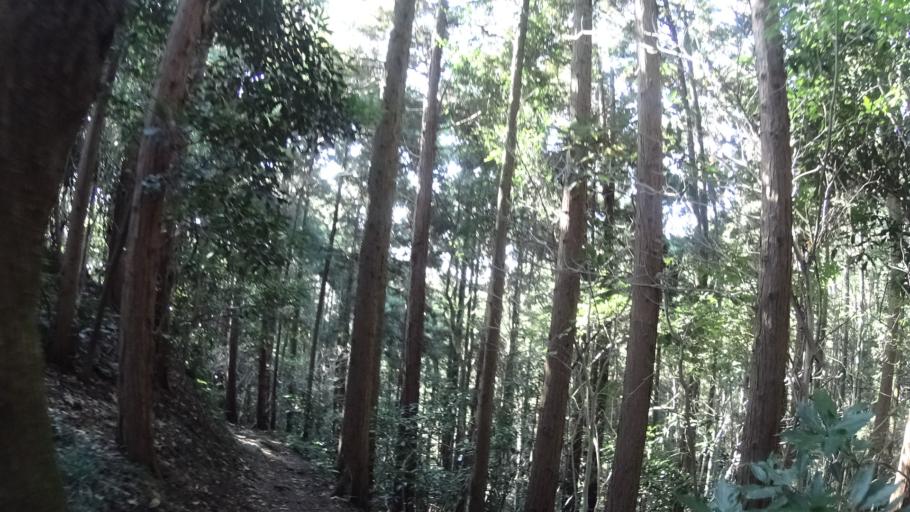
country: JP
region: Kanagawa
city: Hayama
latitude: 35.2845
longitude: 139.6210
